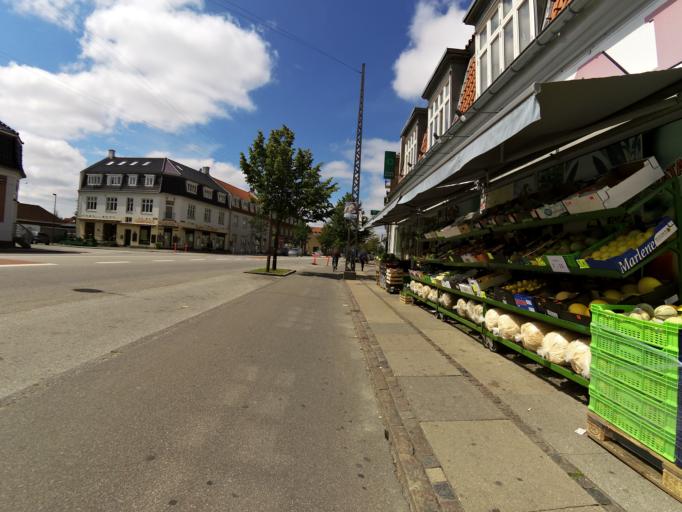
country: DK
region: Capital Region
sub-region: Kobenhavn
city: Vanlose
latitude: 55.7059
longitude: 12.4905
